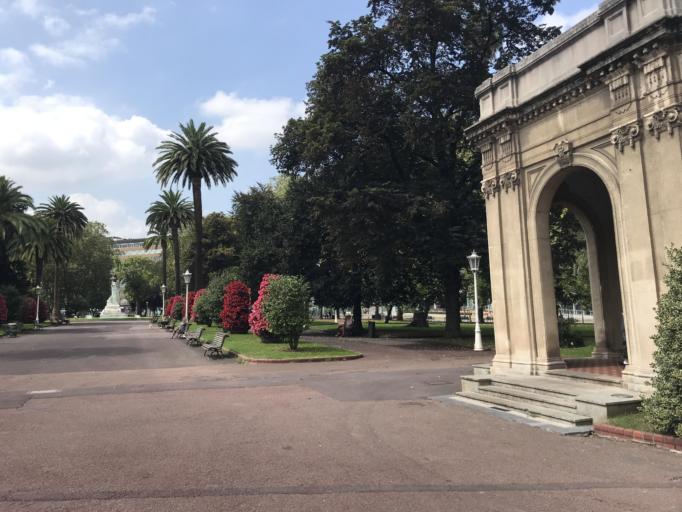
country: ES
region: Basque Country
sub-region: Bizkaia
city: Bilbao
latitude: 43.2658
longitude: -2.9423
